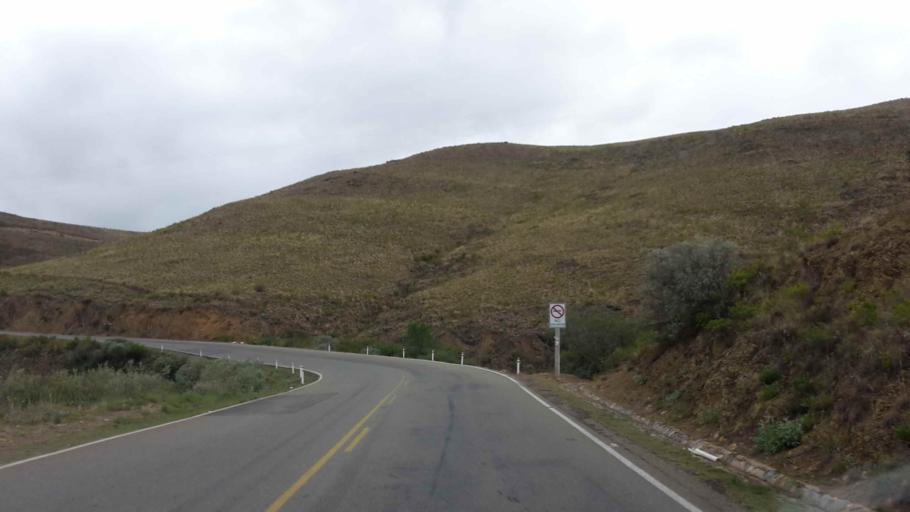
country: BO
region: Cochabamba
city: Punata
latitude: -17.4871
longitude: -65.7800
